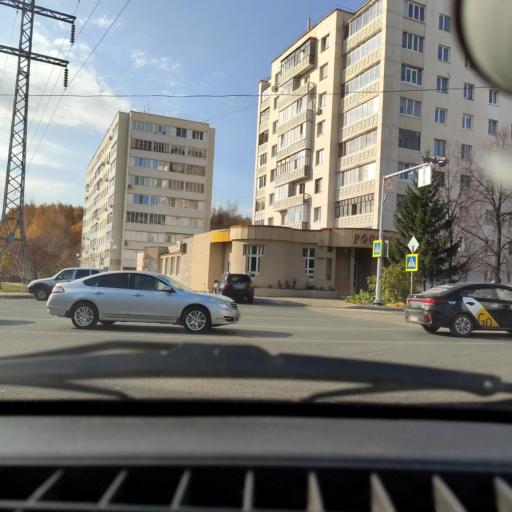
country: RU
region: Bashkortostan
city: Ufa
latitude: 54.7687
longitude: 56.0260
